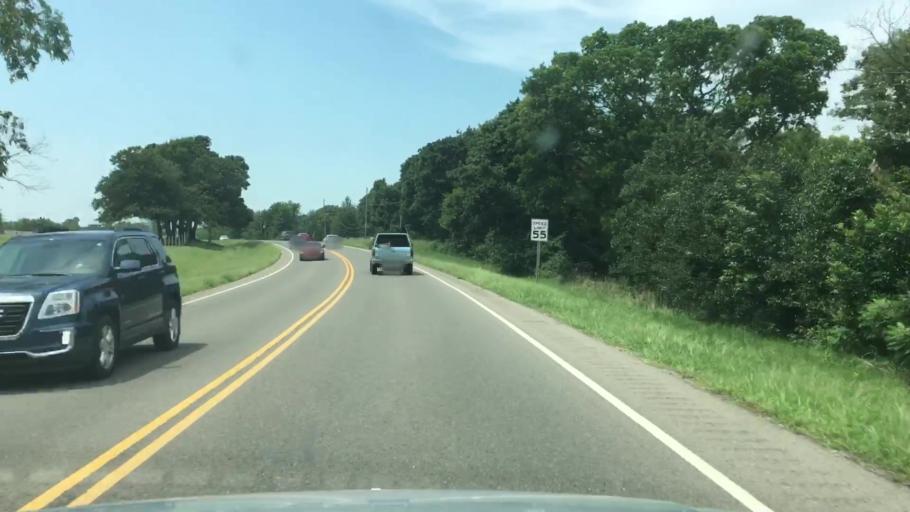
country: US
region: Oklahoma
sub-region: Wagoner County
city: Wagoner
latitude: 35.9422
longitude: -95.2892
